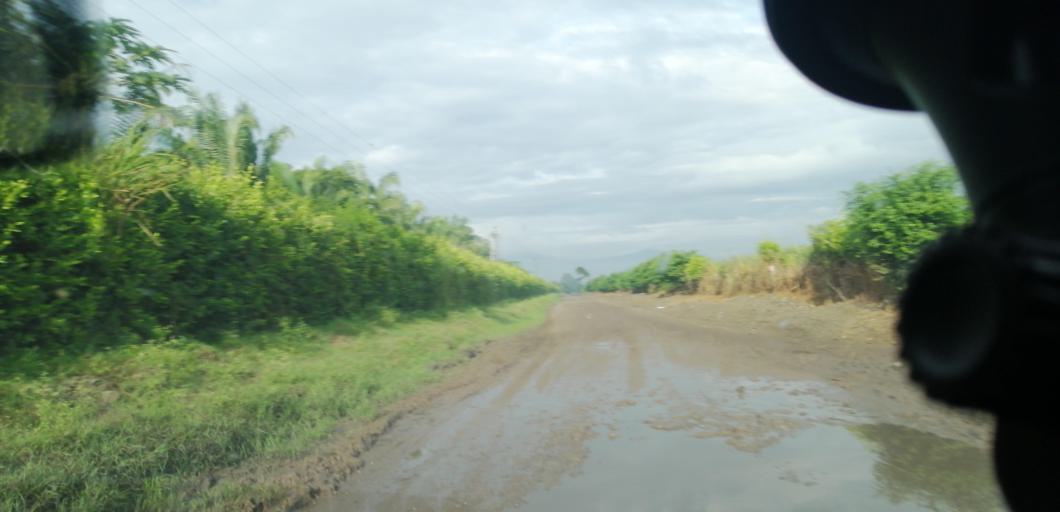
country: CO
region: Valle del Cauca
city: Palmira
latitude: 3.5530
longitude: -76.3637
